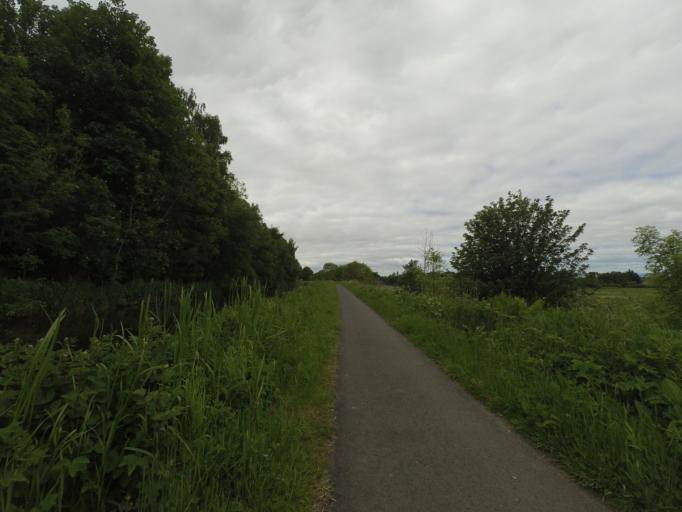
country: GB
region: Scotland
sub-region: West Lothian
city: Linlithgow
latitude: 55.9671
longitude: -3.6284
